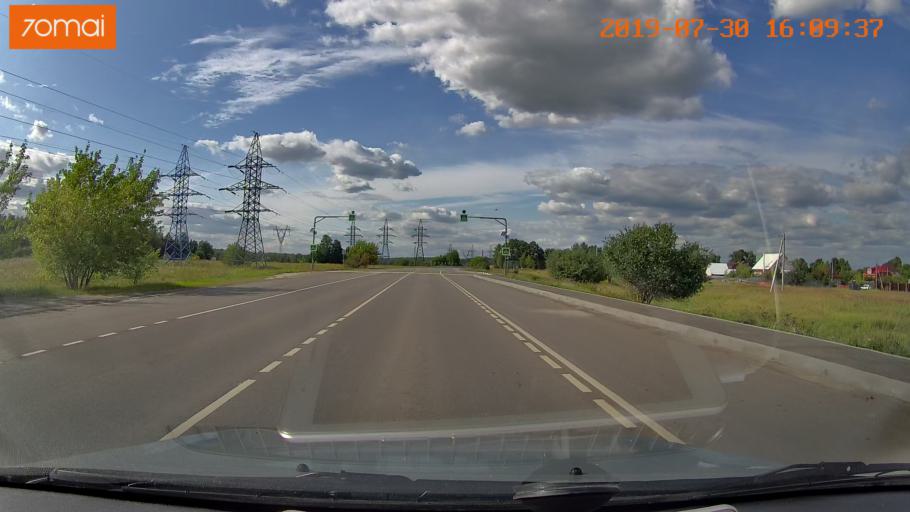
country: RU
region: Moskovskaya
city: Peski
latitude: 55.2547
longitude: 38.7176
